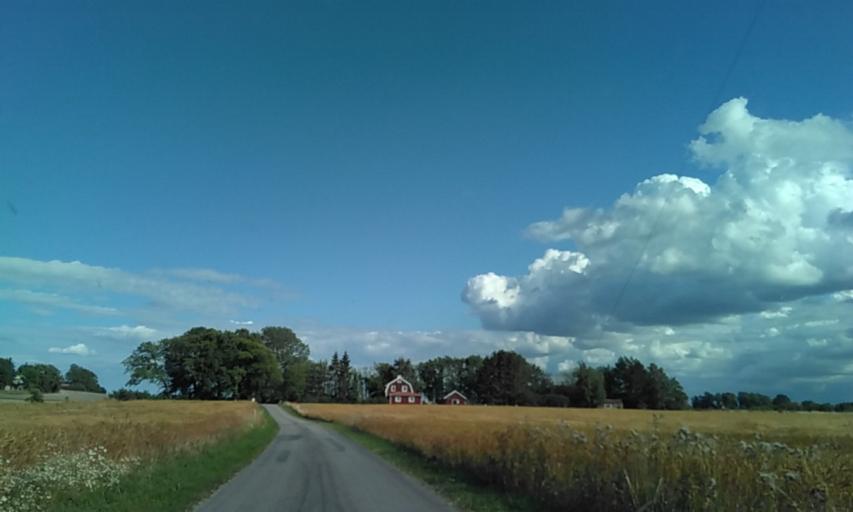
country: SE
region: Vaestra Goetaland
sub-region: Lidkopings Kommun
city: Lidkoping
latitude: 58.5754
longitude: 13.0164
